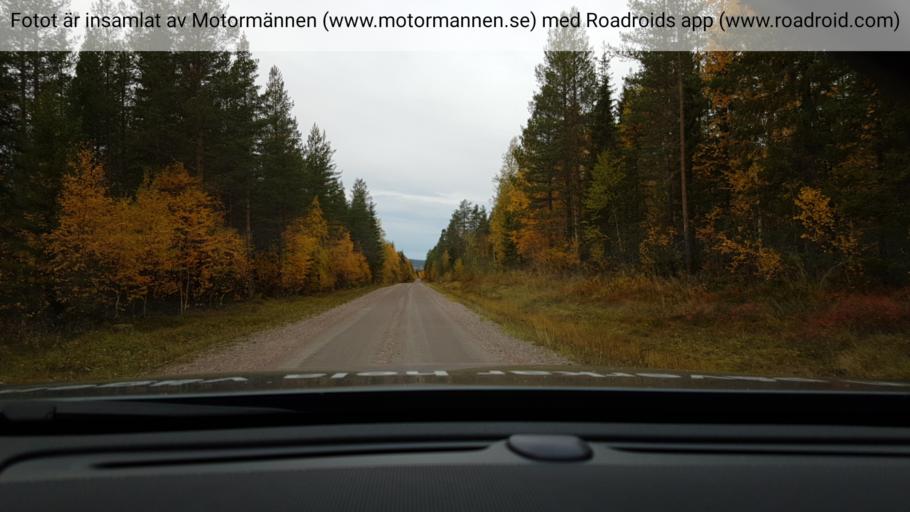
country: SE
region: Norrbotten
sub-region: Overkalix Kommun
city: OEverkalix
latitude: 66.2677
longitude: 23.0100
